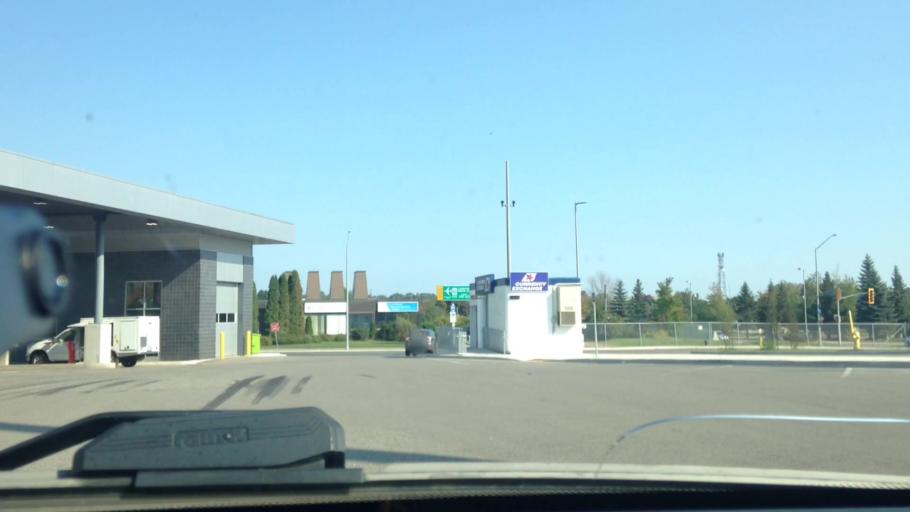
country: CA
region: Ontario
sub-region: Algoma
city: Sault Ste. Marie
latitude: 46.5192
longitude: -84.3489
